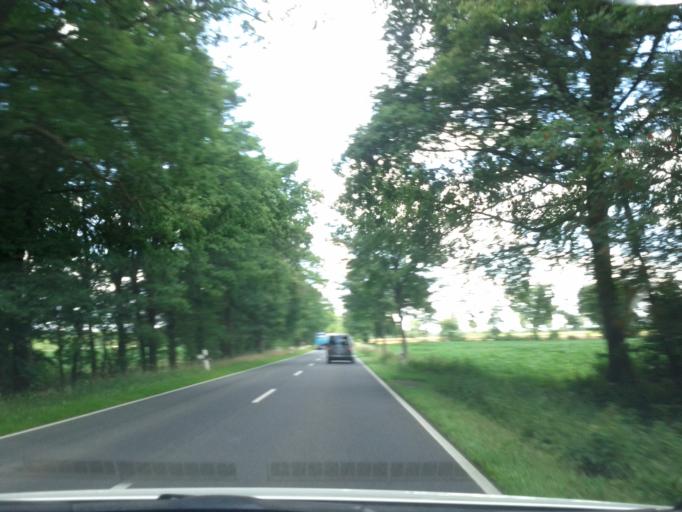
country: DE
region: Lower Saxony
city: Lengenbostel
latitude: 53.3086
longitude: 9.5124
